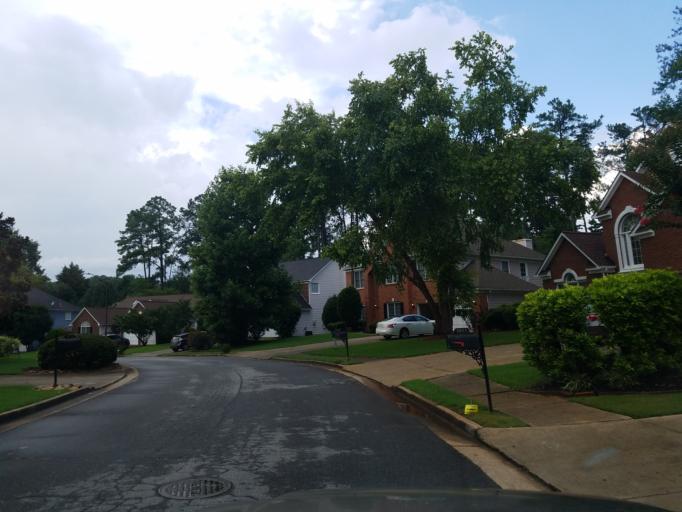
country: US
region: Georgia
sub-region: Cherokee County
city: Woodstock
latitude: 34.0537
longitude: -84.4887
